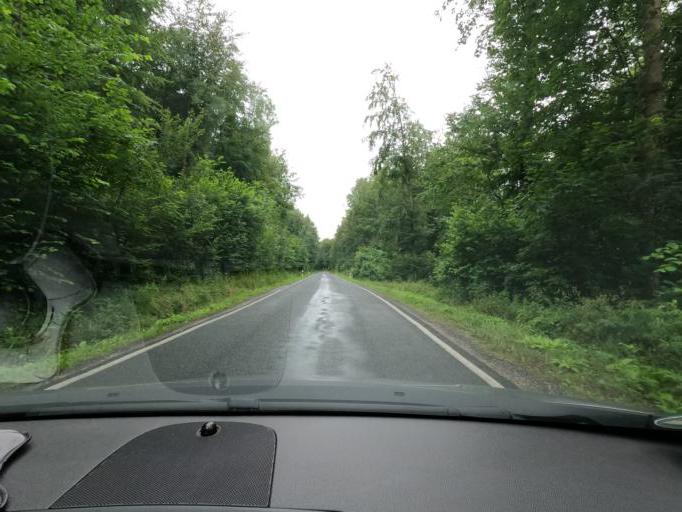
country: DE
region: Thuringia
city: Geisleden
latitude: 51.3400
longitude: 10.1673
